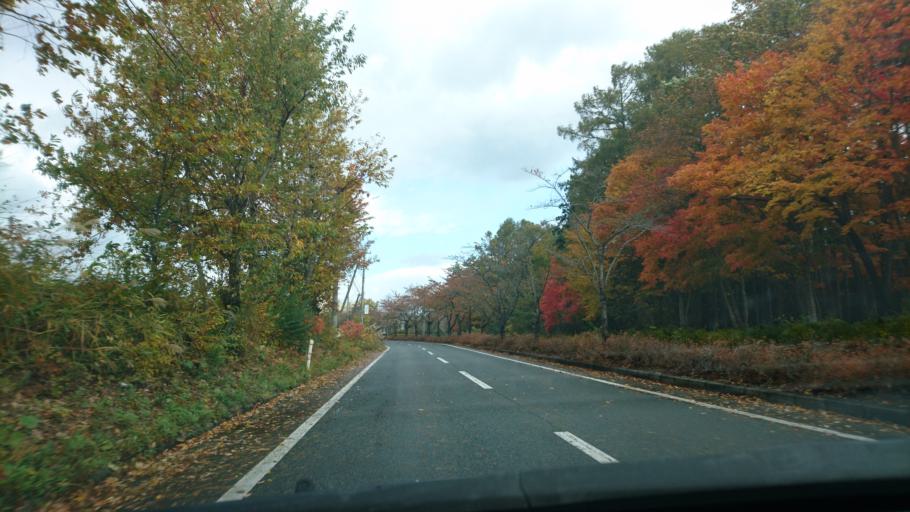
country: JP
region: Iwate
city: Shizukuishi
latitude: 39.6877
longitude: 141.0229
